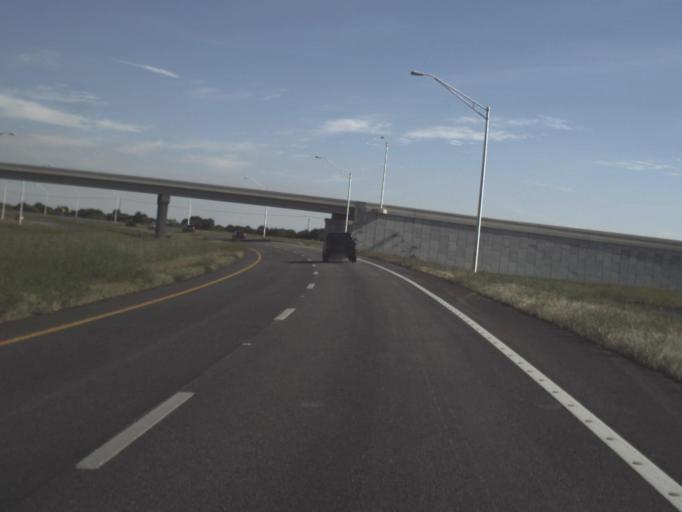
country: US
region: Florida
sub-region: Glades County
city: Moore Haven
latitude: 26.7560
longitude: -81.0826
